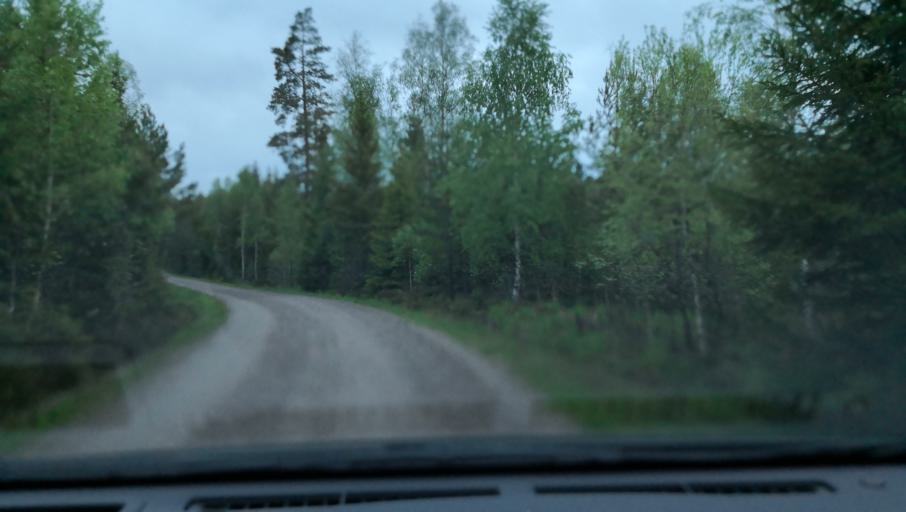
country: SE
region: Uppsala
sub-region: Heby Kommun
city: OEstervala
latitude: 59.9883
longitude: 17.2579
